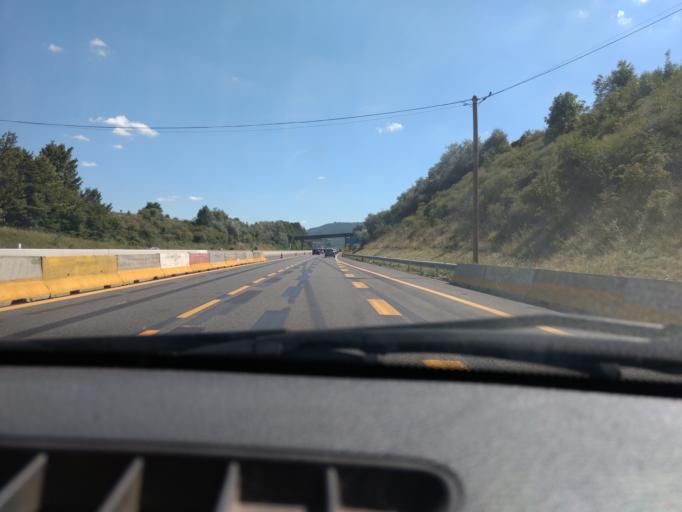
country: FR
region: Auvergne
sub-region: Departement du Puy-de-Dome
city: Aulnat
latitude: 45.7740
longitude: 3.1403
